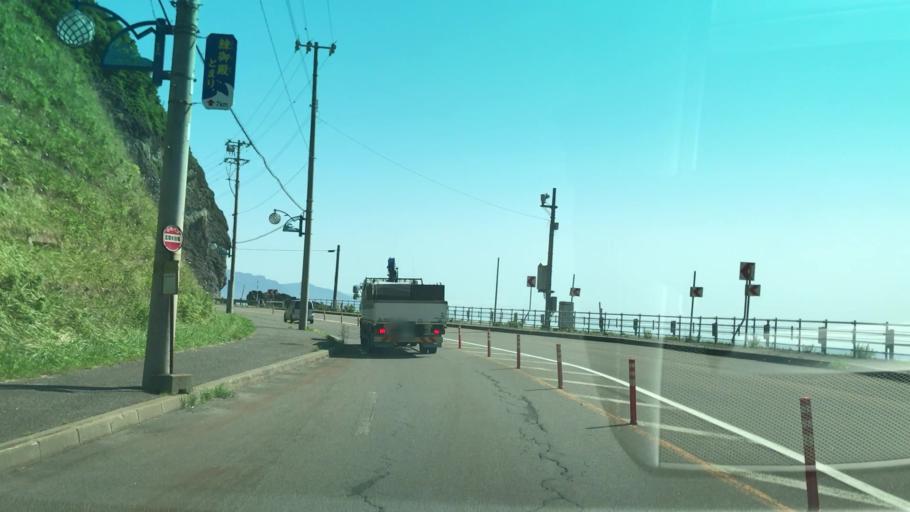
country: JP
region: Hokkaido
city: Iwanai
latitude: 43.1118
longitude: 140.4504
